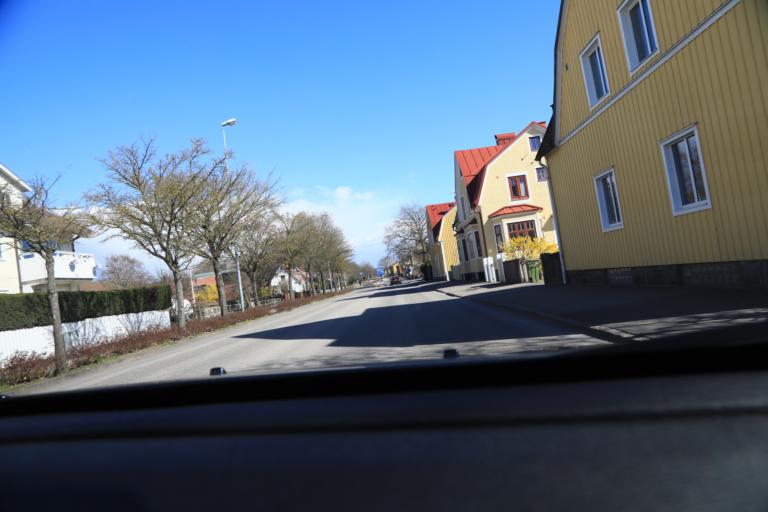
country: SE
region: Halland
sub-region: Varbergs Kommun
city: Varberg
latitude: 57.1038
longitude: 12.2584
